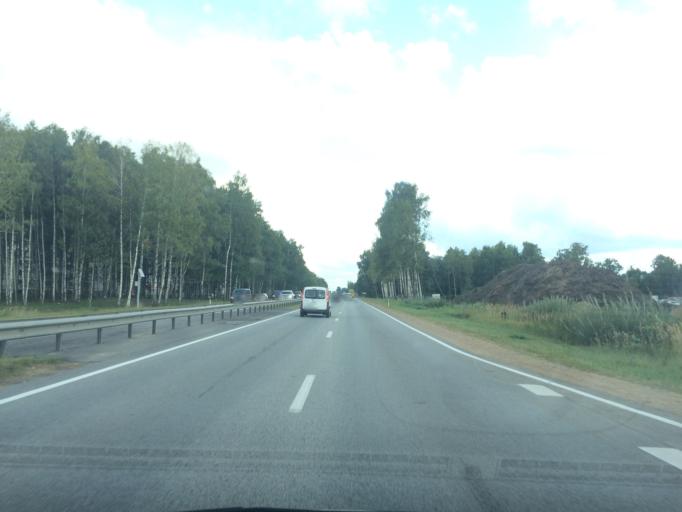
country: LV
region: Salaspils
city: Salaspils
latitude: 56.8551
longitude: 24.3240
